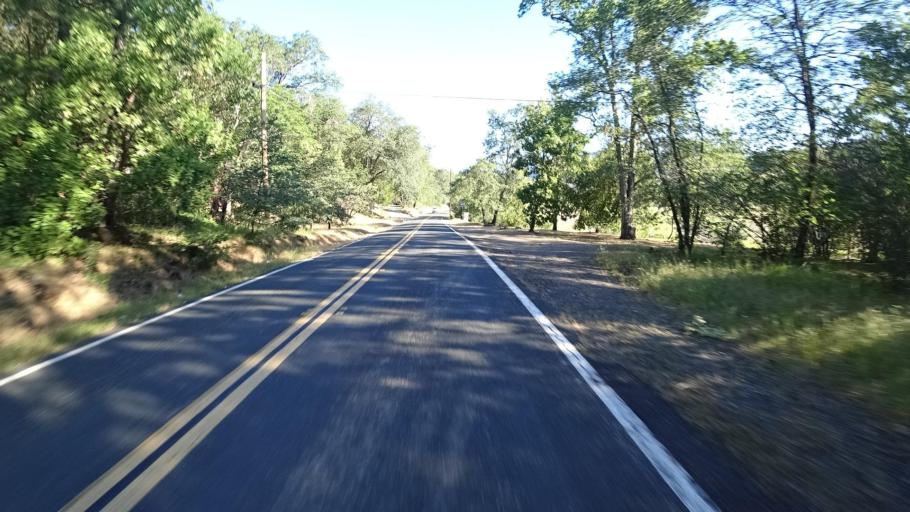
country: US
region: California
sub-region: Lake County
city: Upper Lake
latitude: 39.2319
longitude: -122.9453
